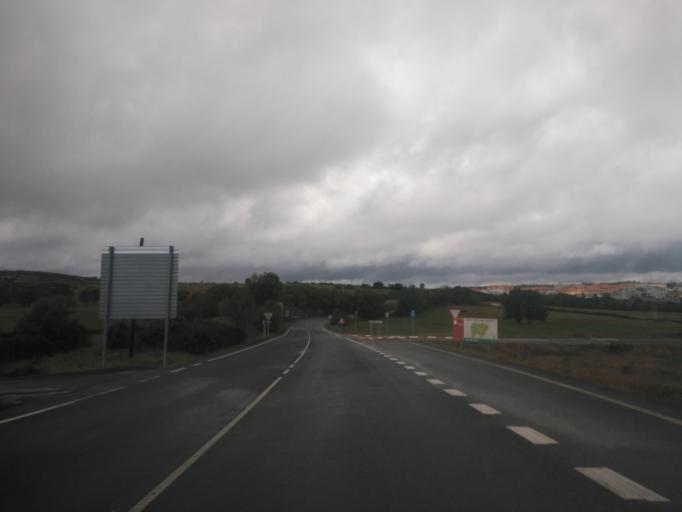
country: ES
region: Castille and Leon
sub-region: Provincia de Salamanca
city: Fuentes de Bejar
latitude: 40.5245
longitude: -5.6734
